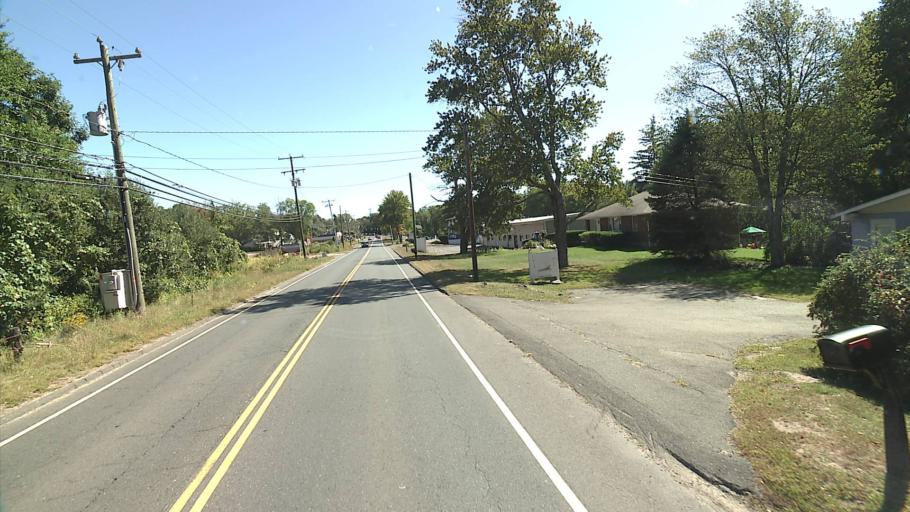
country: US
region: Connecticut
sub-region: New Haven County
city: Prospect
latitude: 41.5055
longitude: -72.9862
